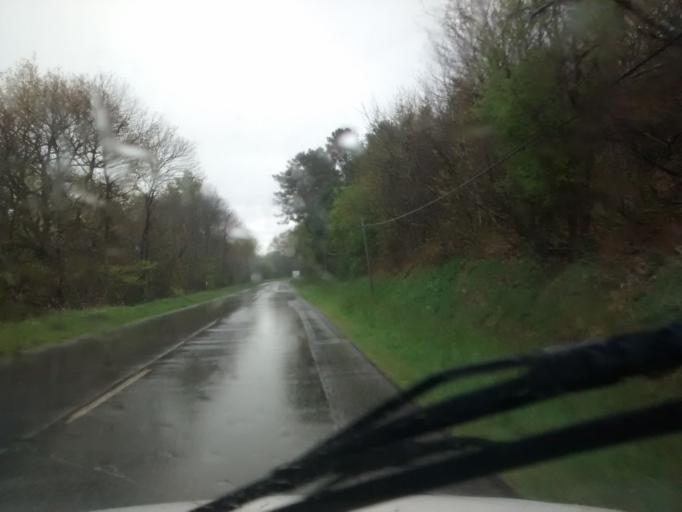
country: FR
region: Brittany
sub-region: Departement du Morbihan
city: Ruffiac
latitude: 47.7768
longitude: -2.3169
